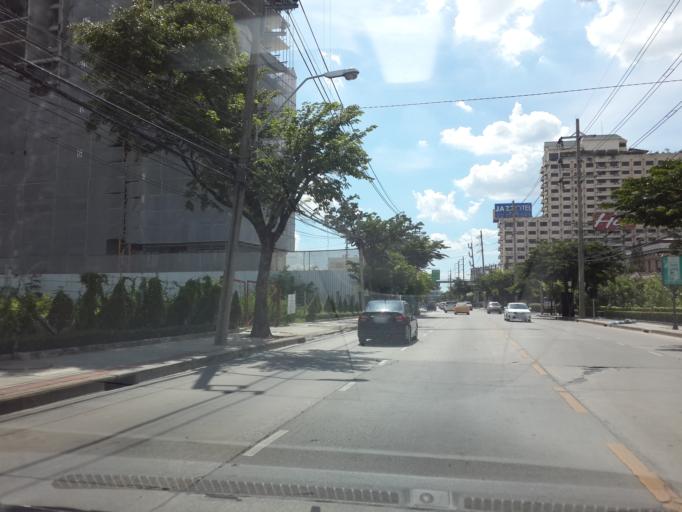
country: TH
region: Bangkok
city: Wang Thonglang
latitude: 13.7676
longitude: 100.5995
